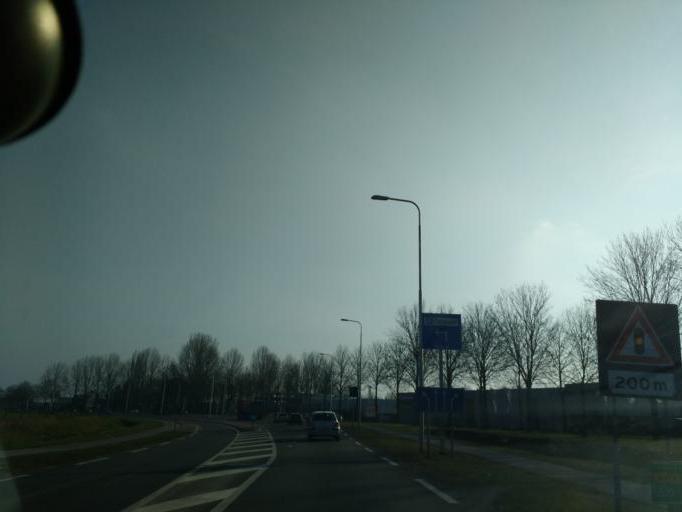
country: NL
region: Gelderland
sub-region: Gemeente Overbetuwe
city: Elst
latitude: 51.8974
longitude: 5.9114
